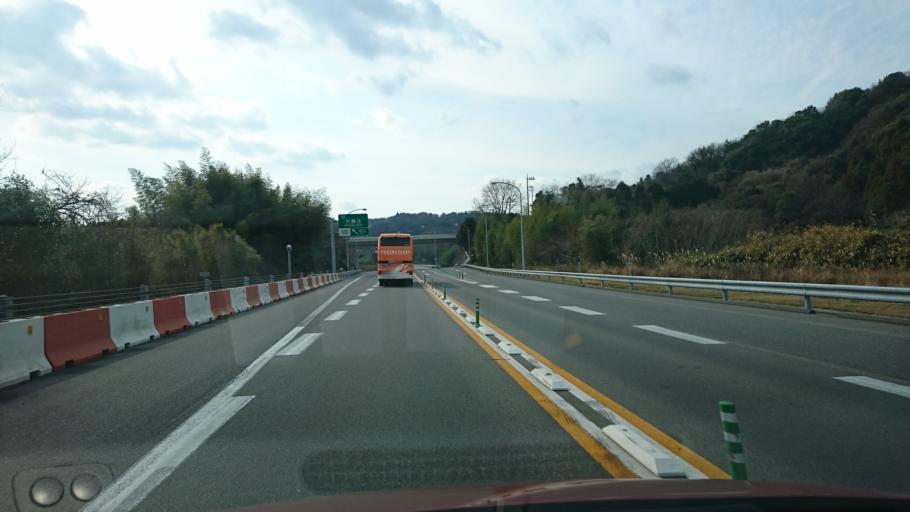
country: JP
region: Hiroshima
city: Innoshima
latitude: 34.1721
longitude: 133.0666
